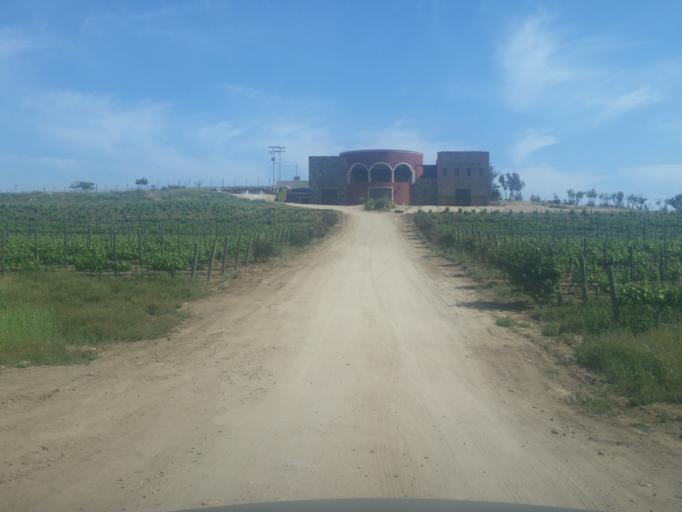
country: MX
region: Baja California
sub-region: Ensenada
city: Rancho Verde
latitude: 32.0182
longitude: -116.6644
